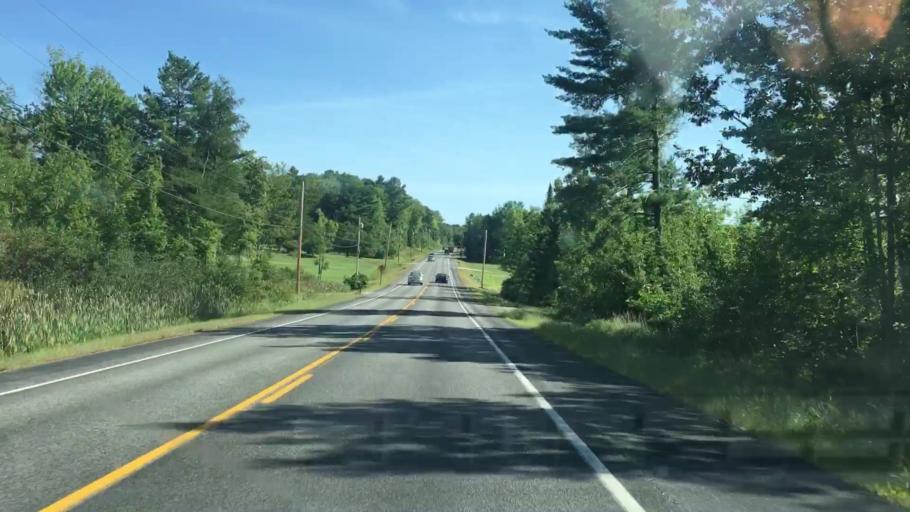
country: US
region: Maine
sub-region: Androscoggin County
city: Lisbon
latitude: 44.0416
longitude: -70.0764
